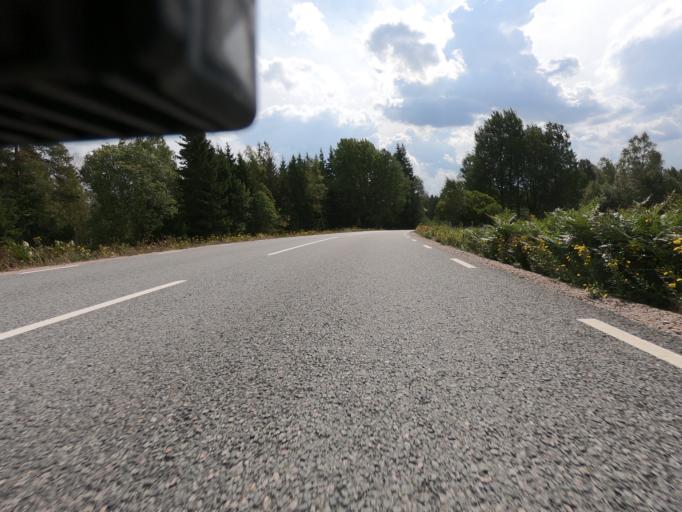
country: SE
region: Joenkoeping
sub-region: Vetlanda Kommun
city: Landsbro
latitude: 57.2763
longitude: 14.9142
